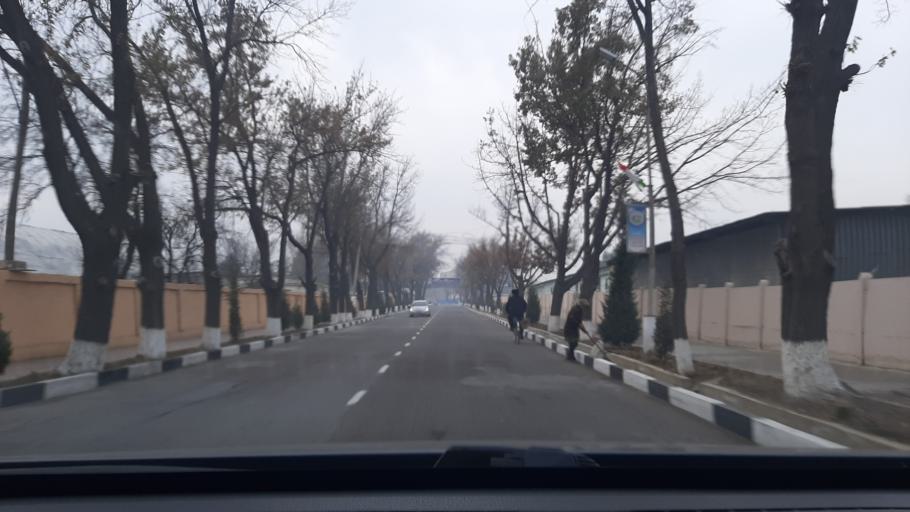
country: TJ
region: Viloyati Sughd
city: Chkalov
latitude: 40.2379
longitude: 69.6894
